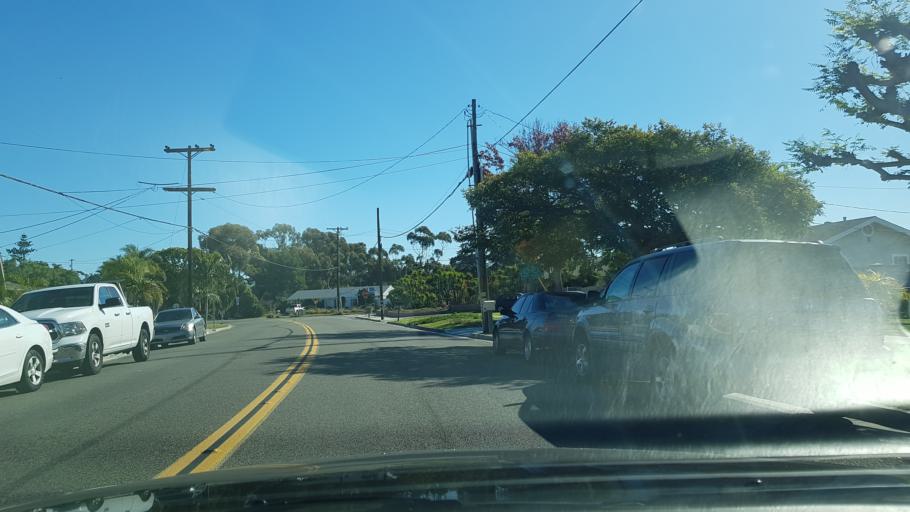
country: US
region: California
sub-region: San Diego County
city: Oceanside
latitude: 33.2045
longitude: -117.3511
